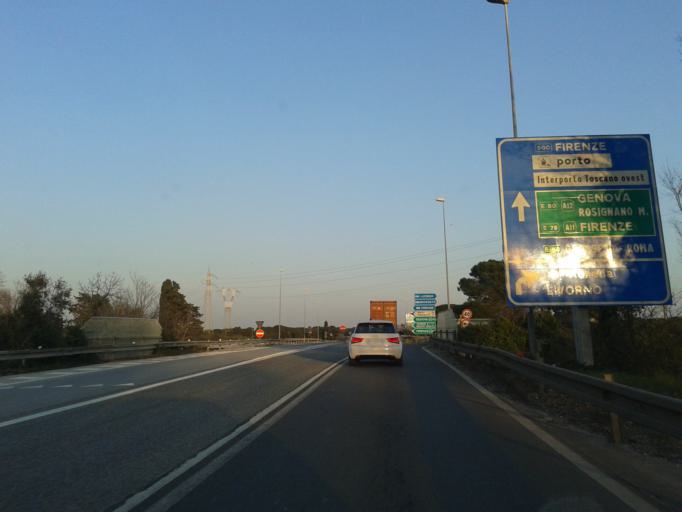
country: IT
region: Tuscany
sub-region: Provincia di Livorno
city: Livorno
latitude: 43.5833
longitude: 10.3521
